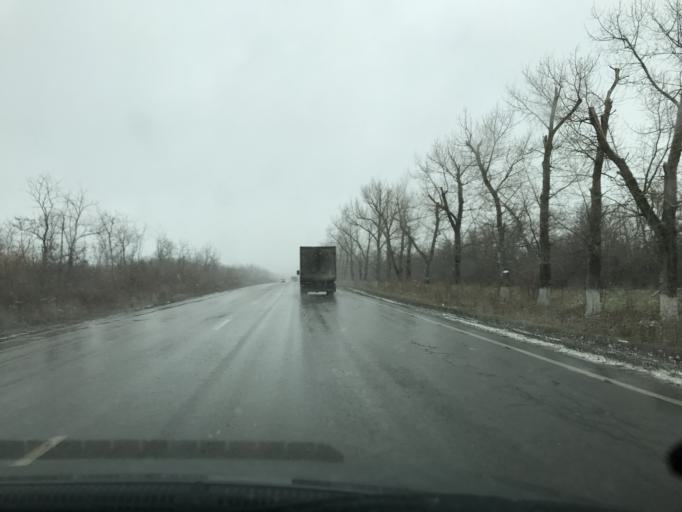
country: RU
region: Rostov
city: Bataysk
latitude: 47.0593
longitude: 39.8194
